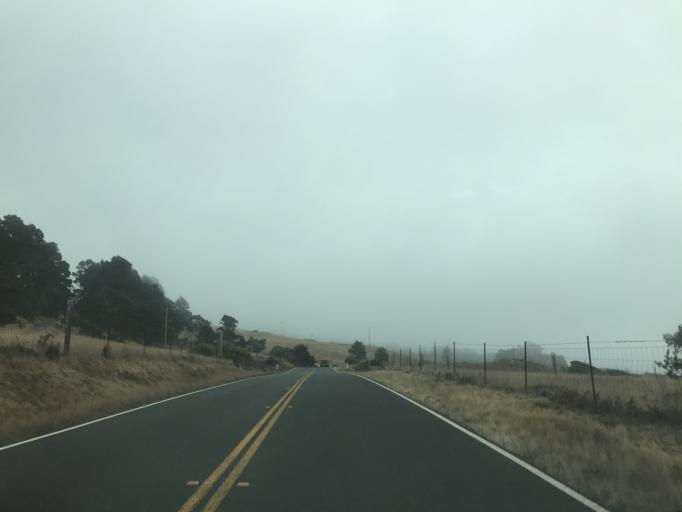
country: US
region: California
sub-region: Sonoma County
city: Sea Ranch
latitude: 38.6568
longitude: -123.4026
